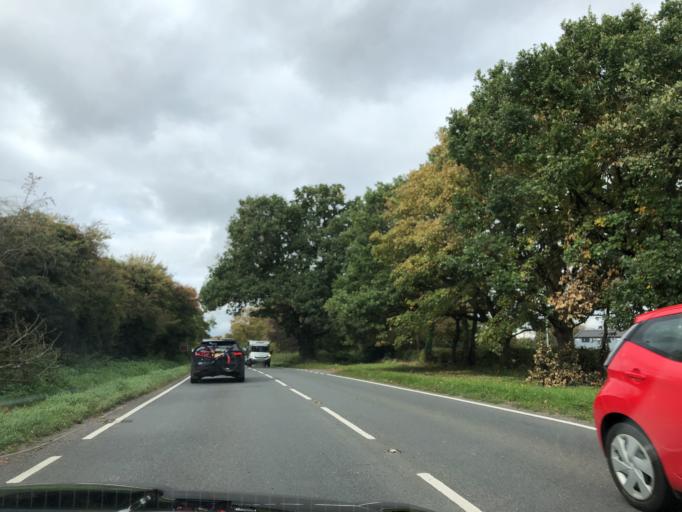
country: GB
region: England
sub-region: Warwickshire
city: Royal Leamington Spa
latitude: 52.3187
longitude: -1.5432
